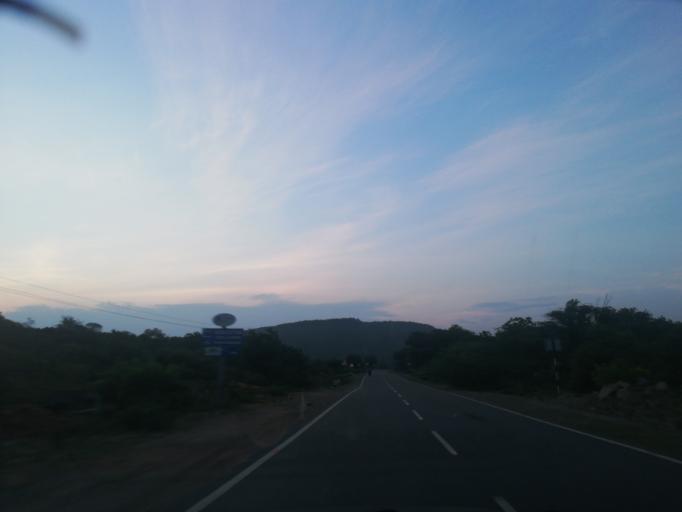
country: IN
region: Andhra Pradesh
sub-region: Guntur
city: Macherla
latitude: 16.6667
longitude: 79.2831
